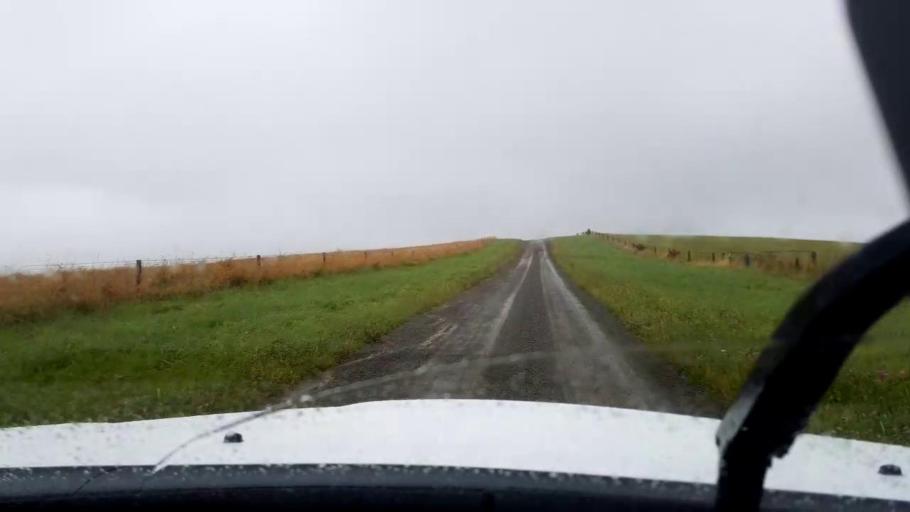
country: NZ
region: Canterbury
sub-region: Timaru District
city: Pleasant Point
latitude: -44.1672
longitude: 171.1696
